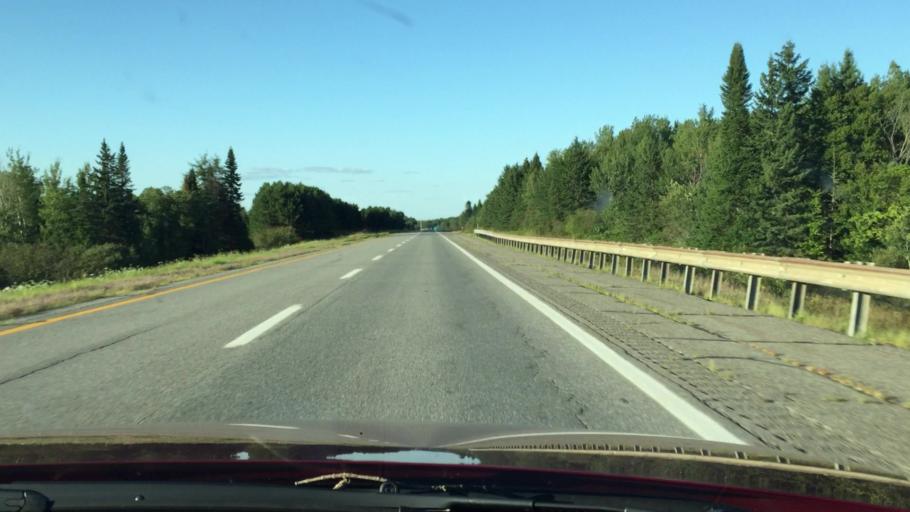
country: US
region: Maine
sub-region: Penobscot County
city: Patten
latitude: 45.8589
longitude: -68.4216
